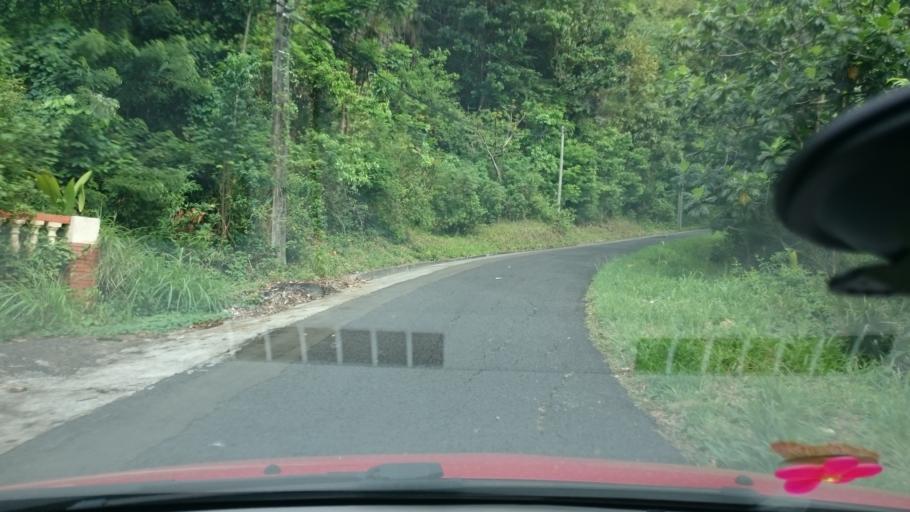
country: MQ
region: Martinique
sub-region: Martinique
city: Riviere-Pilote
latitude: 14.4901
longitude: -60.9086
